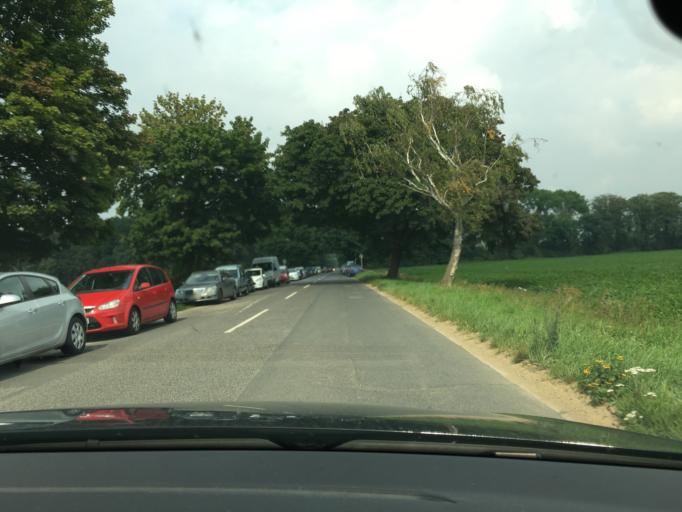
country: DE
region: North Rhine-Westphalia
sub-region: Regierungsbezirk Koln
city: Merzenich
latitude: 50.8702
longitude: 6.5691
